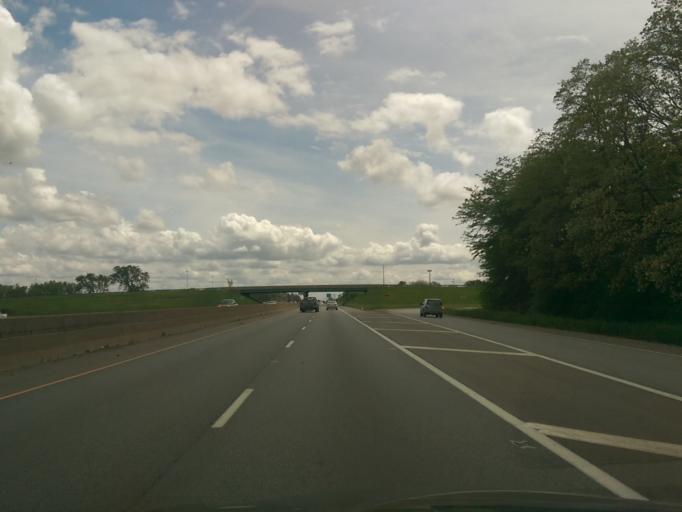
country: US
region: Indiana
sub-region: Lake County
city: Highland
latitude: 41.5902
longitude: -87.4330
